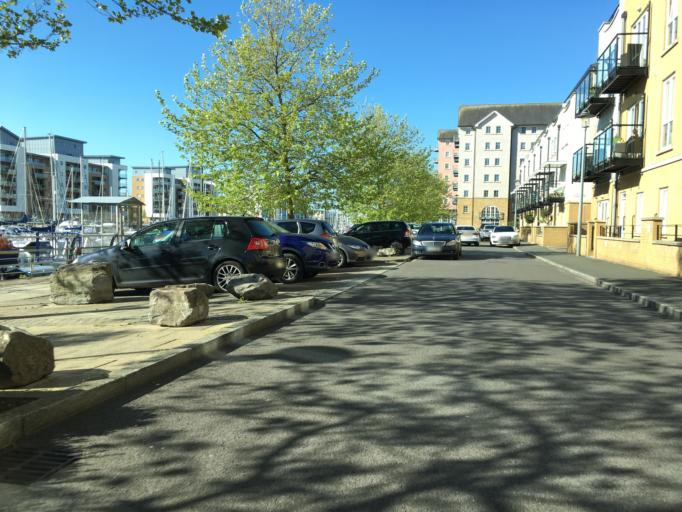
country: GB
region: England
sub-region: North Somerset
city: Portishead
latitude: 51.4917
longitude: -2.7586
